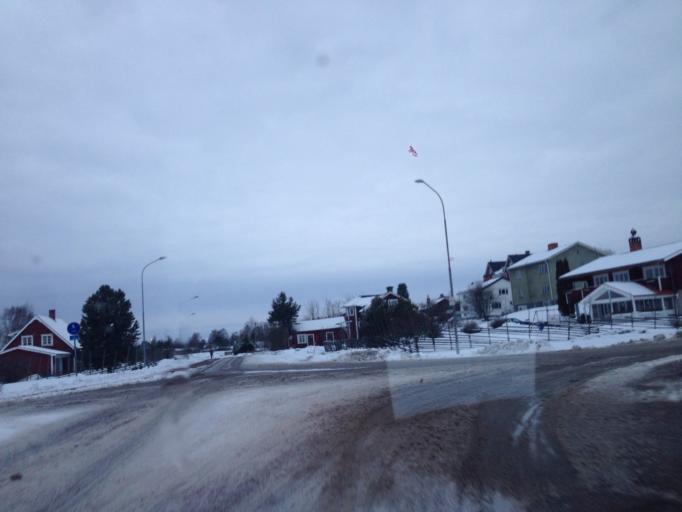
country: SE
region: Dalarna
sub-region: Mora Kommun
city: Mora
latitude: 61.0059
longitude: 14.5786
